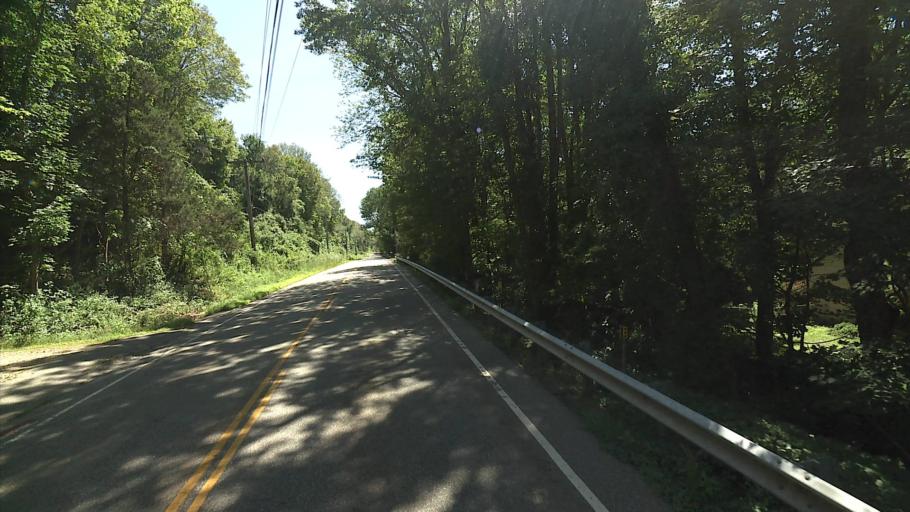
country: US
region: Connecticut
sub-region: New London County
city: Baltic
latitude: 41.6695
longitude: -72.0859
